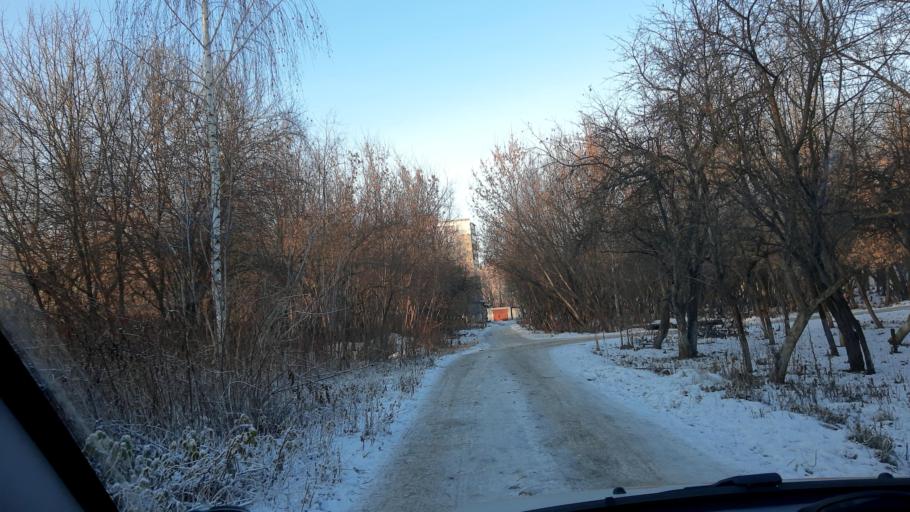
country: RU
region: Nizjnij Novgorod
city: Gorbatovka
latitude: 56.2651
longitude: 43.8693
